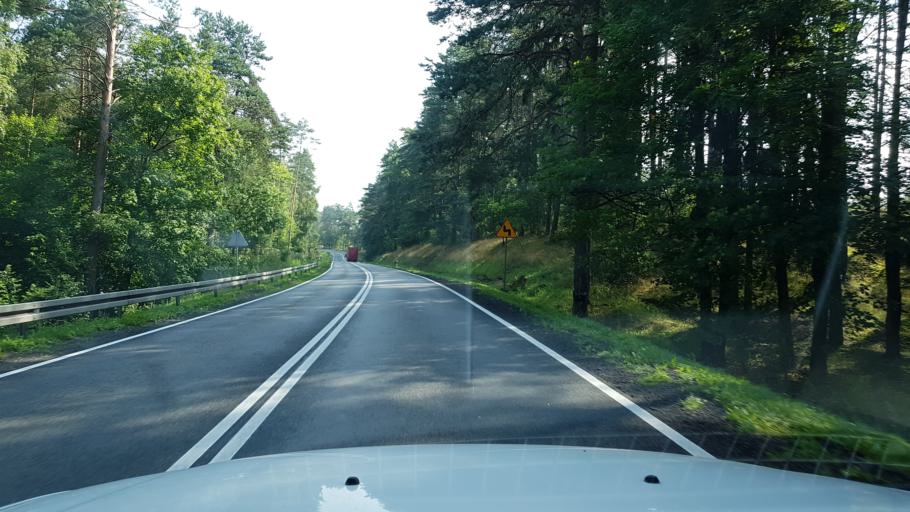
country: PL
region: West Pomeranian Voivodeship
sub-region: Powiat drawski
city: Kalisz Pomorski
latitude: 53.2901
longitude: 15.9495
